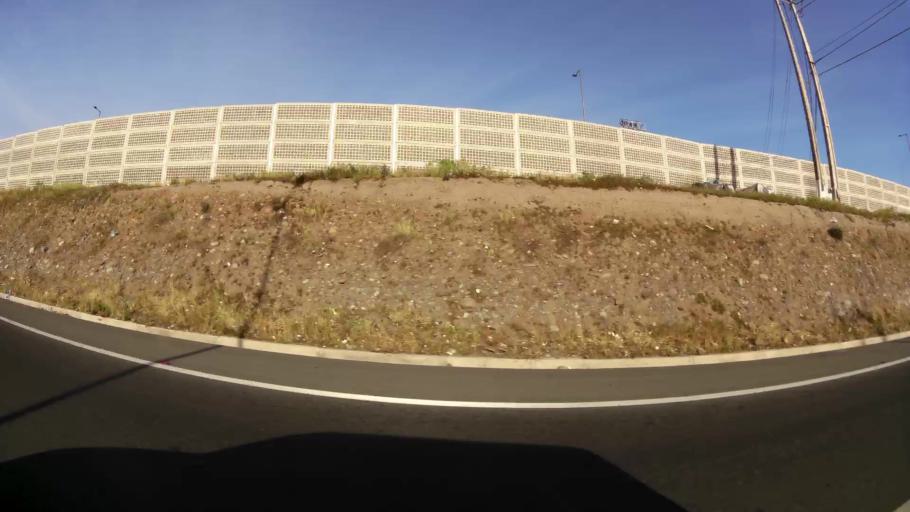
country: CL
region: Santiago Metropolitan
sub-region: Provincia de Santiago
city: La Pintana
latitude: -33.5841
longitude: -70.6107
